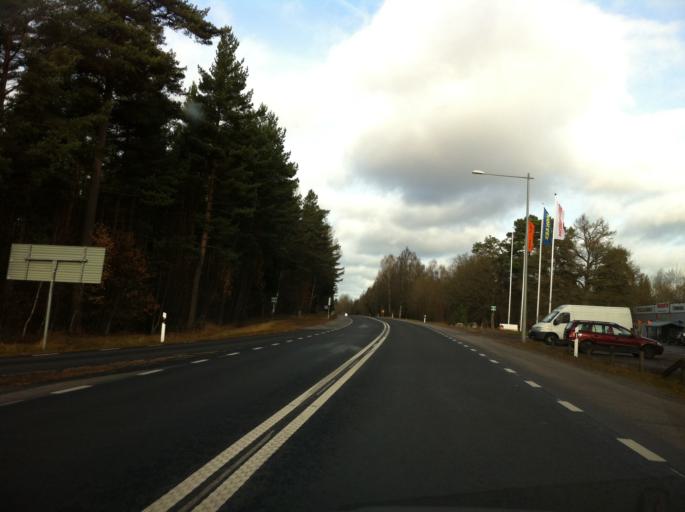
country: SE
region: Kronoberg
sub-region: Vaxjo Kommun
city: Gemla
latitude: 56.7939
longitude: 14.6303
